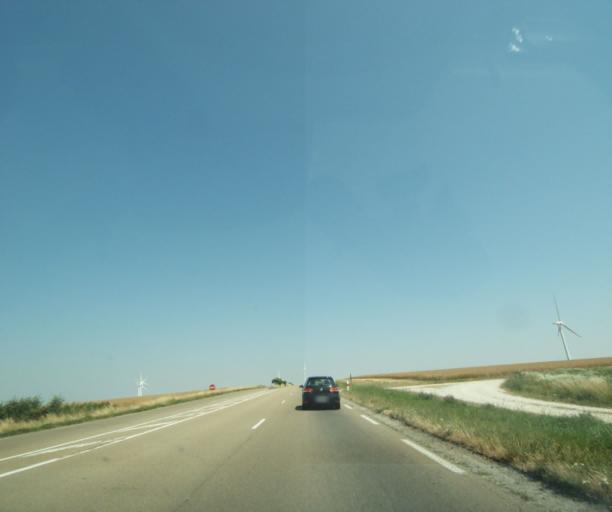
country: FR
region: Champagne-Ardenne
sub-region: Departement de la Marne
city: Vitry-le-Francois
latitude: 48.7898
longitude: 4.5792
